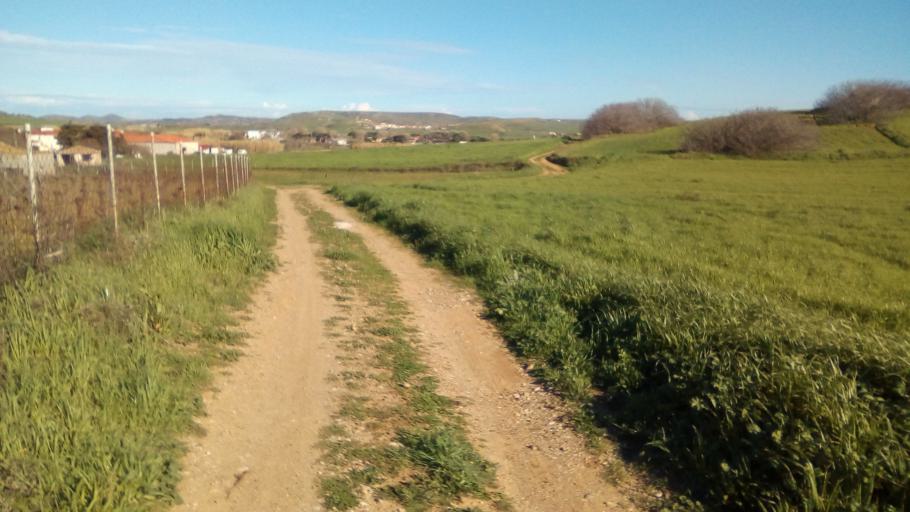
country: GR
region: North Aegean
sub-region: Nomos Lesvou
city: Myrina
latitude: 39.9327
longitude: 25.2342
